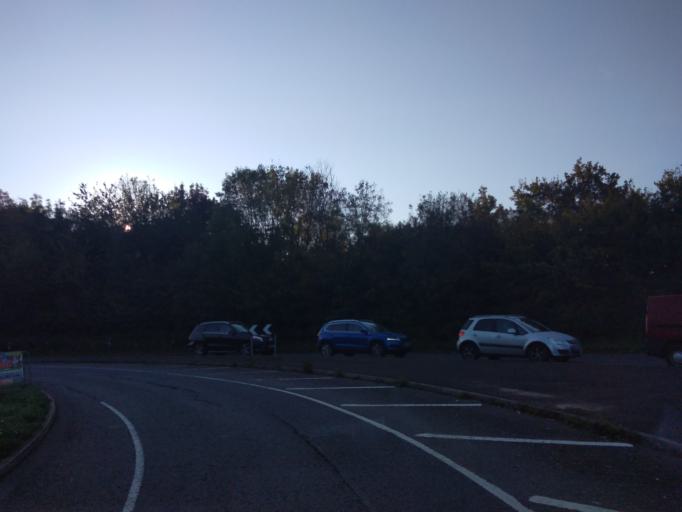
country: GB
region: England
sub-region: West Sussex
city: Goring-by-Sea
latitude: 50.8379
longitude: -0.4511
